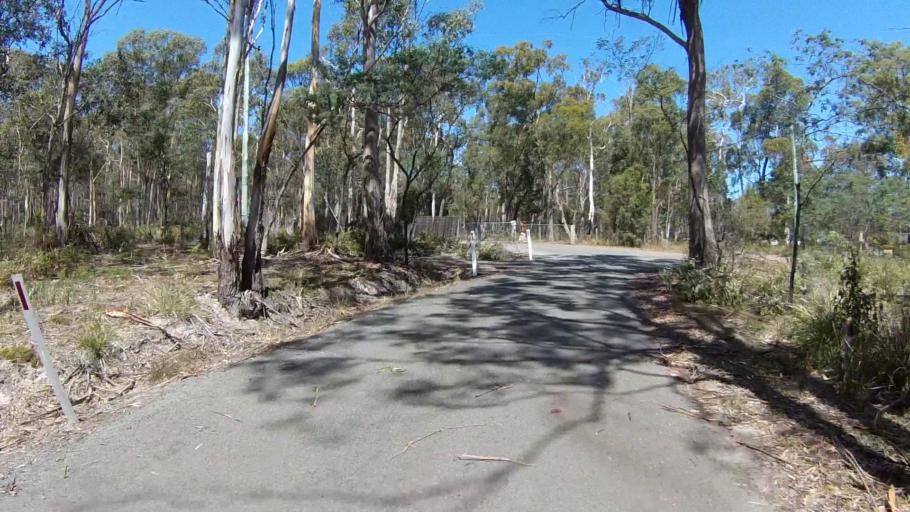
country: AU
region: Tasmania
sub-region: Clarence
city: Sandford
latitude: -42.9641
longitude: 147.4793
